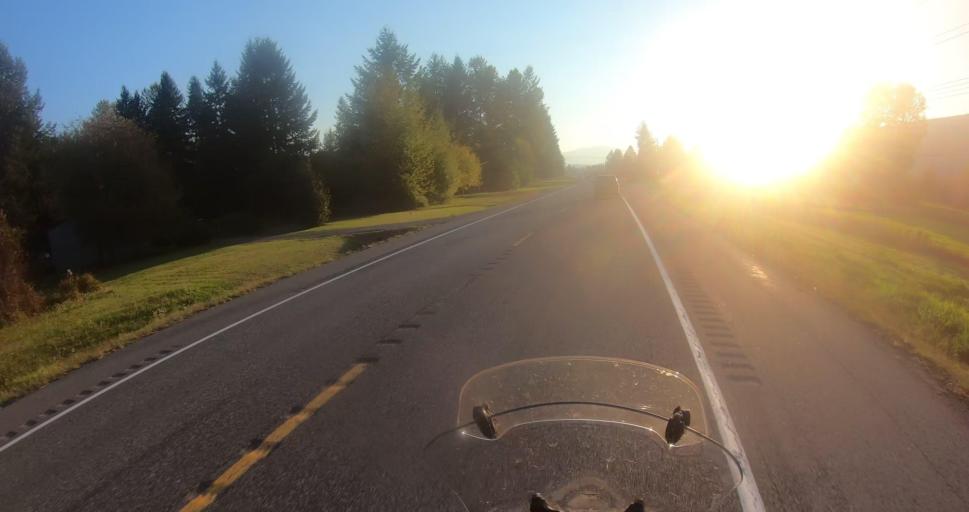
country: US
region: Washington
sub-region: Lewis County
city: Morton
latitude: 46.5261
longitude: -122.1401
